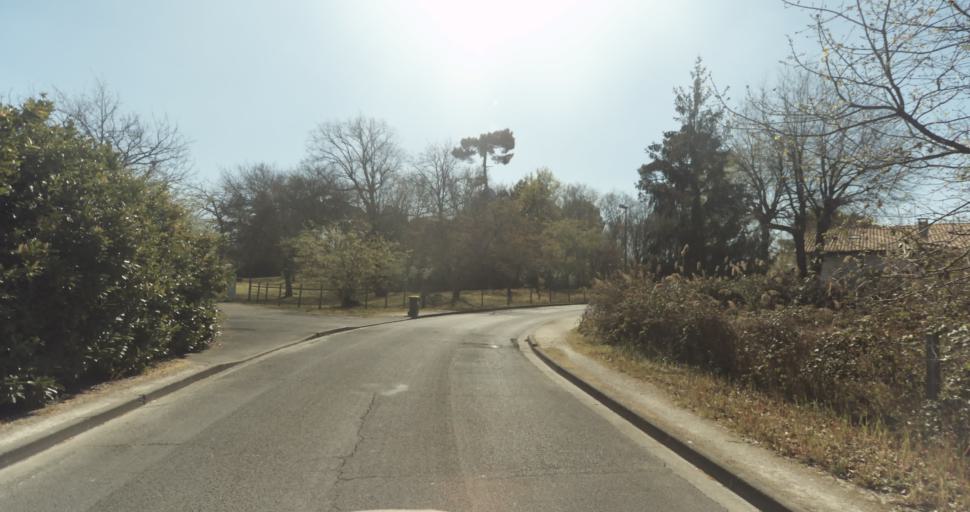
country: FR
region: Aquitaine
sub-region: Departement de la Gironde
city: Martignas-sur-Jalle
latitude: 44.8094
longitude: -0.7828
